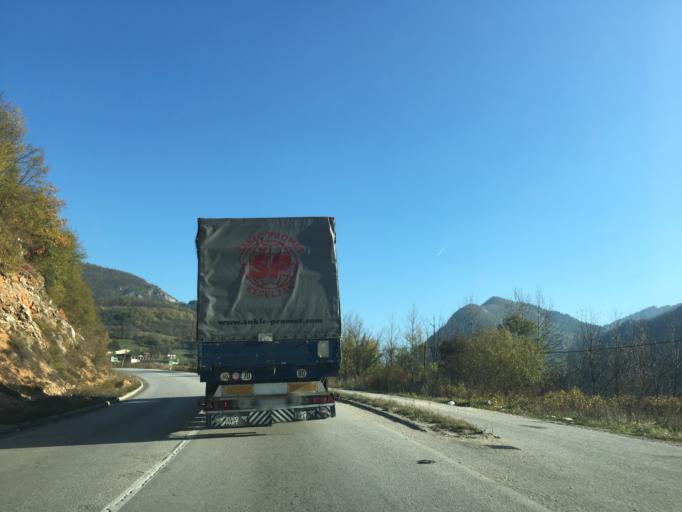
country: BA
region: Republika Srpska
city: Pale
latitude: 43.8421
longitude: 18.4791
